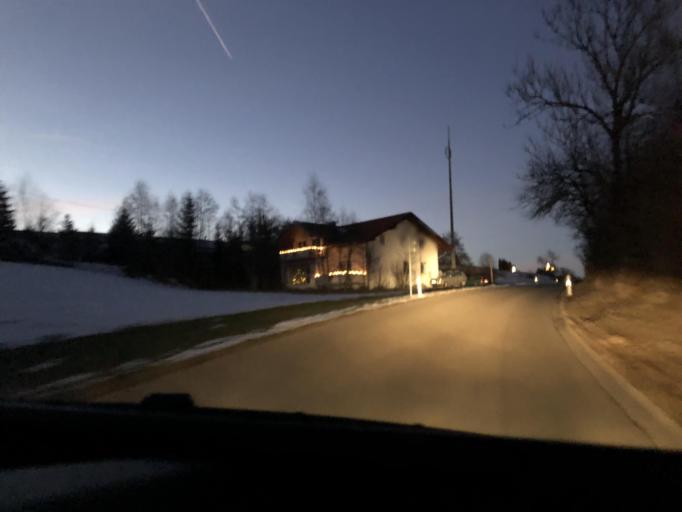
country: DE
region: Bavaria
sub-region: Swabia
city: Waltenhofen
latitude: 47.6753
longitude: 10.3164
